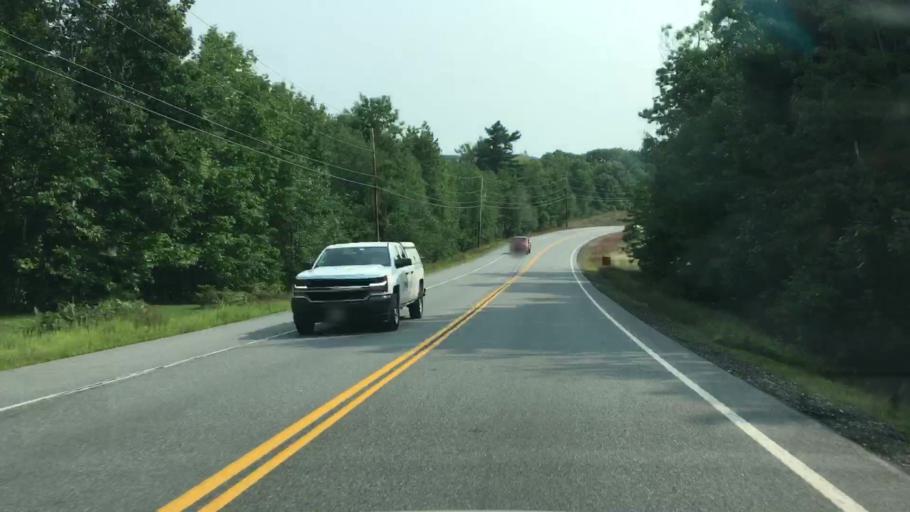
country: US
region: Maine
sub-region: Oxford County
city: Hebron
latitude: 44.2518
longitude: -70.4379
